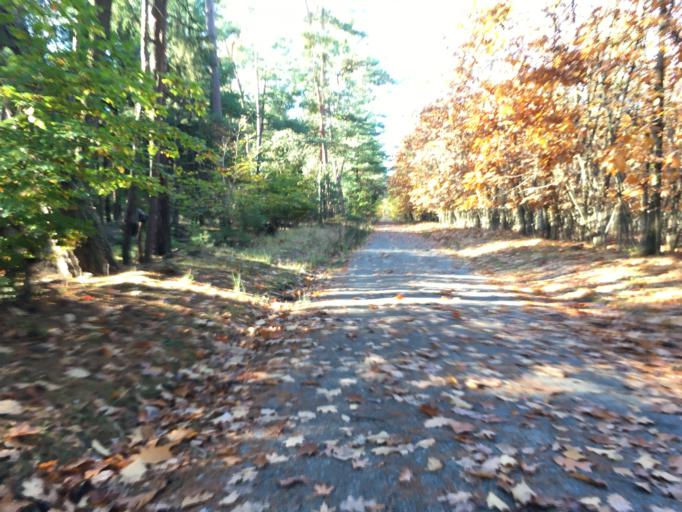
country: DE
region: Hesse
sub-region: Regierungsbezirk Darmstadt
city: Einhausen
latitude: 49.6440
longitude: 8.5284
